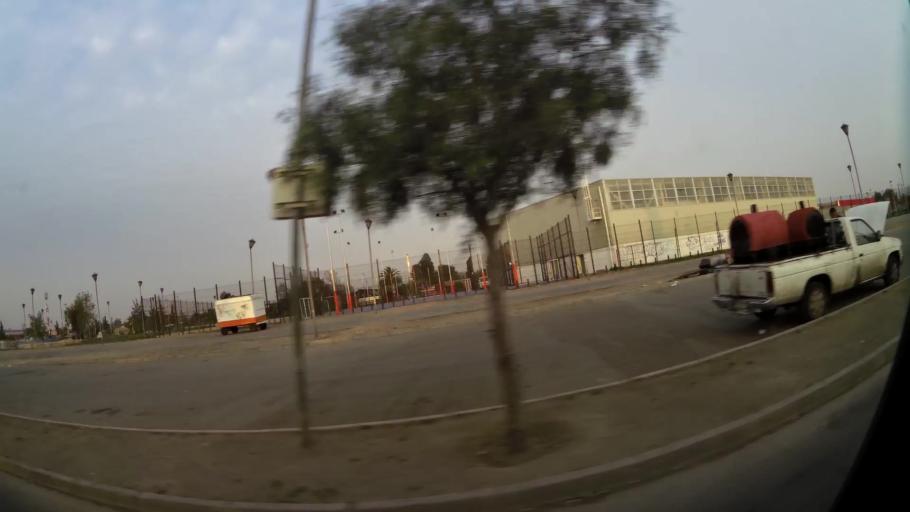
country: CL
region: Santiago Metropolitan
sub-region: Provincia de Santiago
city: Lo Prado
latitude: -33.5145
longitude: -70.7791
